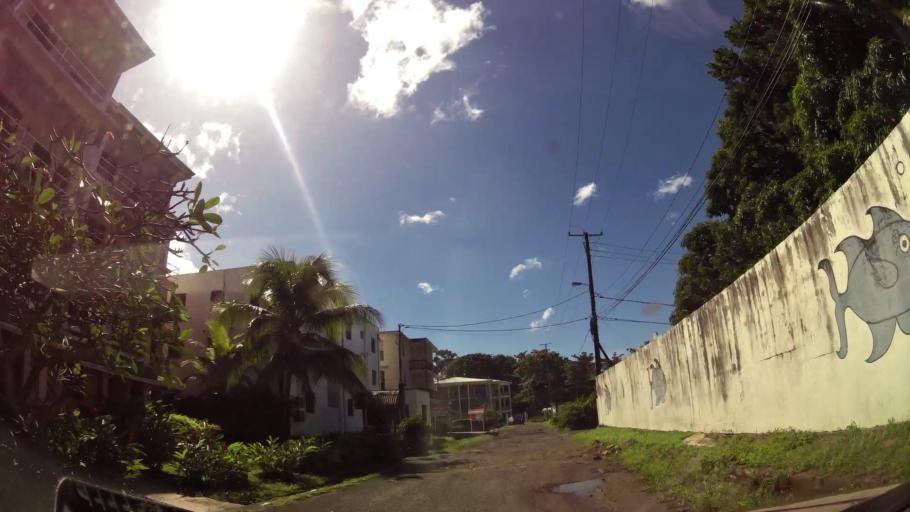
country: DM
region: Saint John
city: Portsmouth
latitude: 15.5590
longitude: -61.4588
